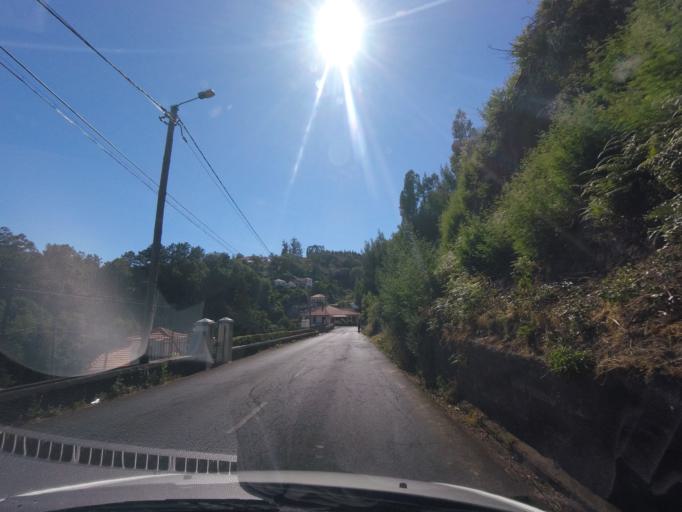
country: PT
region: Madeira
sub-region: Santa Cruz
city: Camacha
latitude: 32.6868
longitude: -16.8506
